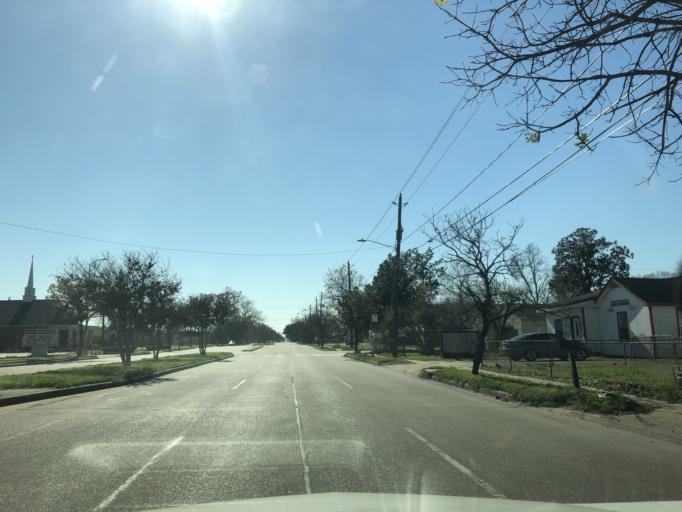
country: US
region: Texas
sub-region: Harris County
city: Houston
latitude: 29.8290
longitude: -95.3021
